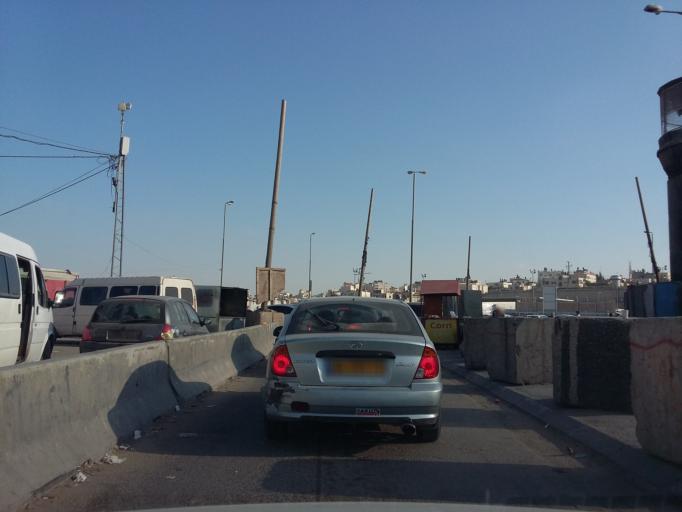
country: PS
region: West Bank
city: Ar Ram wa Dahiyat al Barid
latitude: 31.8635
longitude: 35.2277
